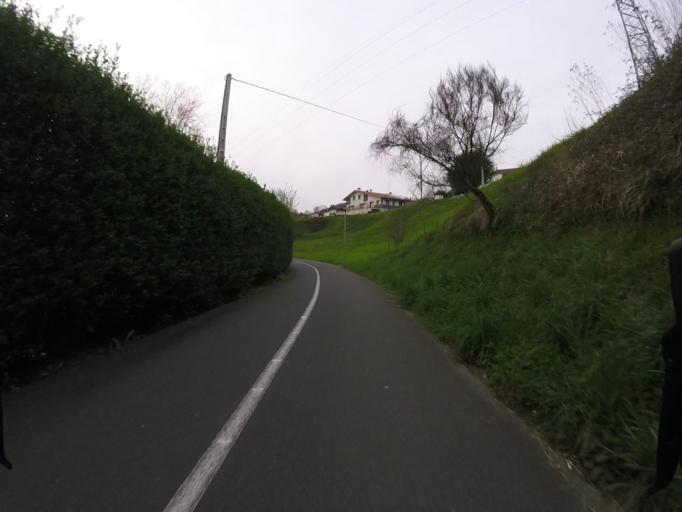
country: ES
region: Basque Country
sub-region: Provincia de Guipuzcoa
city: Lezo
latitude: 43.2943
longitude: -1.8502
